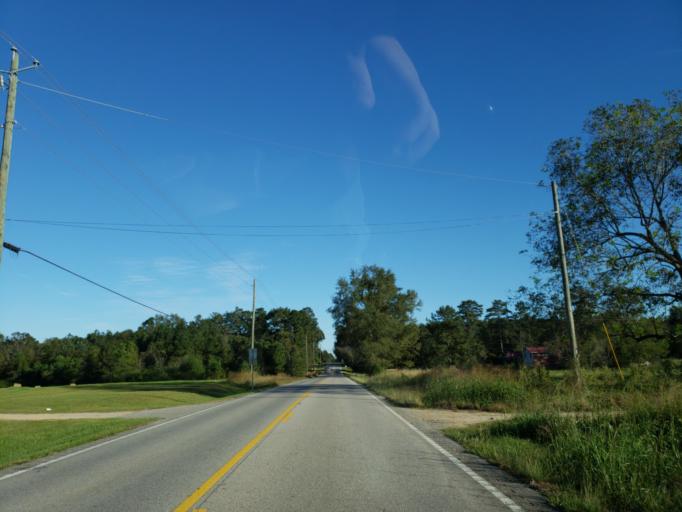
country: US
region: Mississippi
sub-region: Perry County
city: Richton
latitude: 31.3566
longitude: -88.9584
